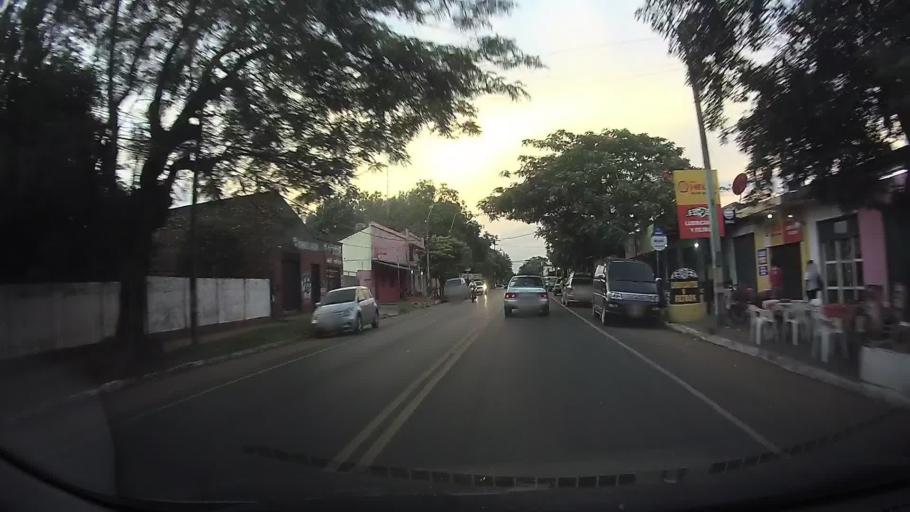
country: PY
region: Central
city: Ita
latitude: -25.5089
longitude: -57.3567
